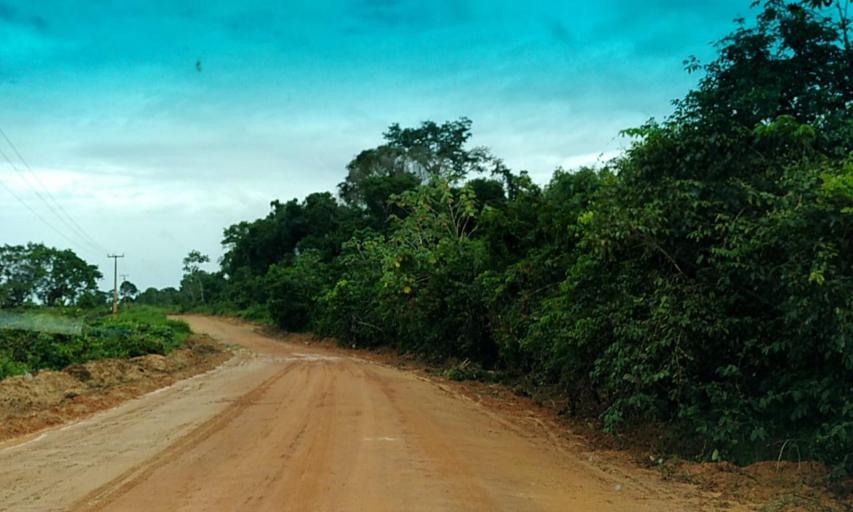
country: BR
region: Para
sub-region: Senador Jose Porfirio
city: Senador Jose Porfirio
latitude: -3.0136
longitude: -51.6810
